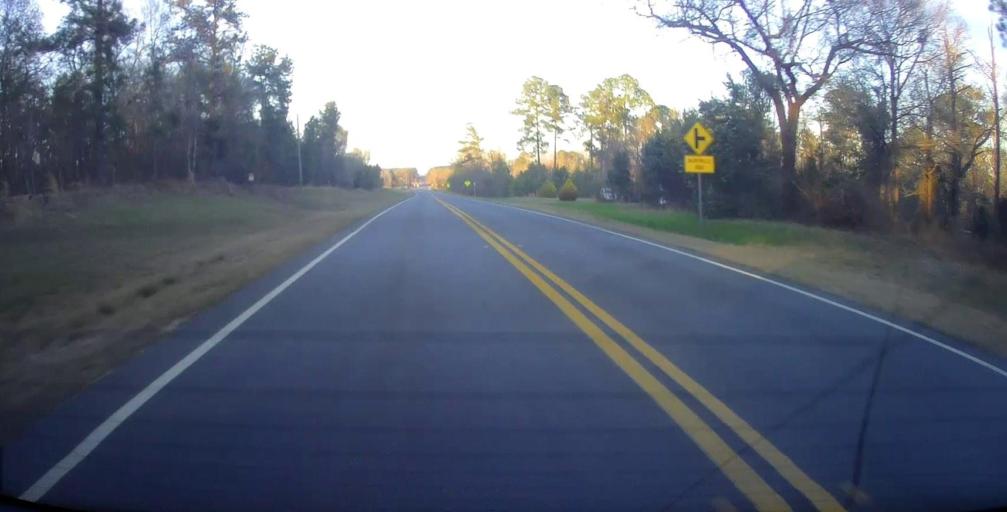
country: US
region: Georgia
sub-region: Laurens County
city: Dublin
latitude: 32.3985
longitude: -82.9749
